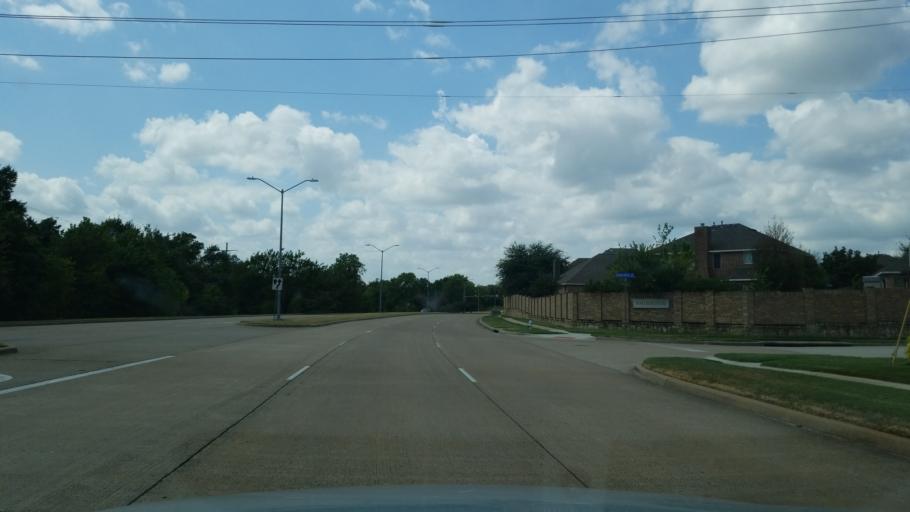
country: US
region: Texas
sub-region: Tarrant County
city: Euless
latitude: 32.8688
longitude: -97.0878
